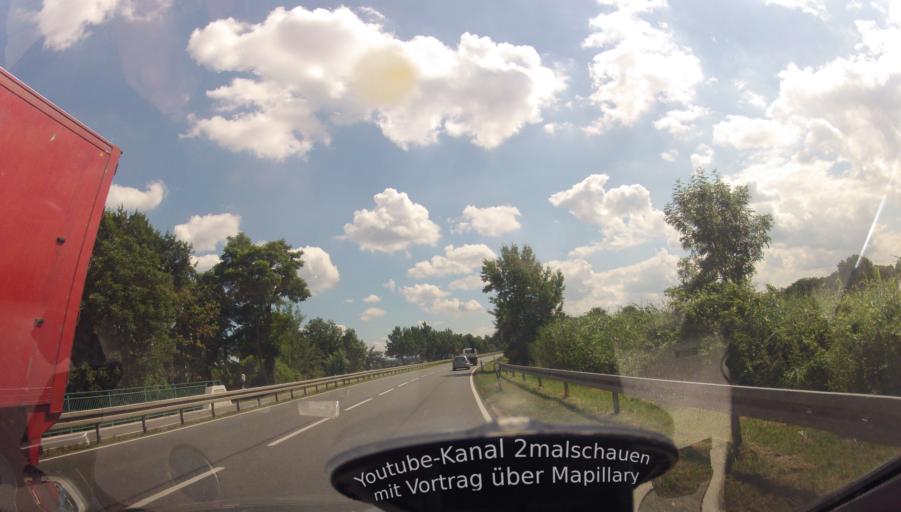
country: DE
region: Saxony
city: Torgau
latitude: 51.5377
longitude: 13.0036
